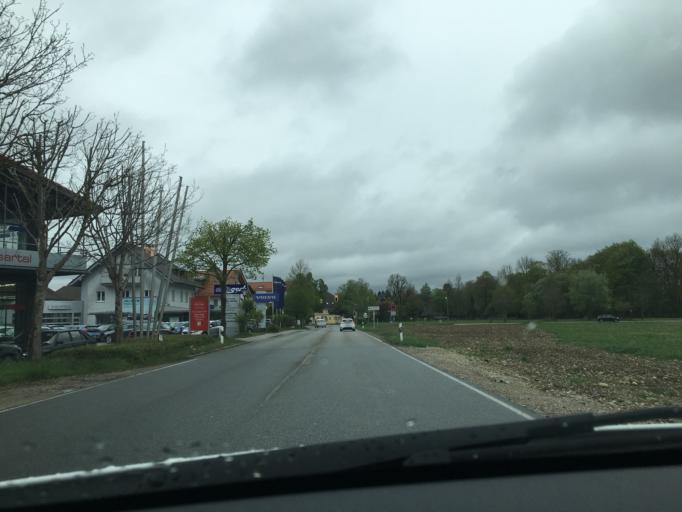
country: DE
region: Bavaria
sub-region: Upper Bavaria
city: Baierbrunn
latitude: 48.0177
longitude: 11.4841
